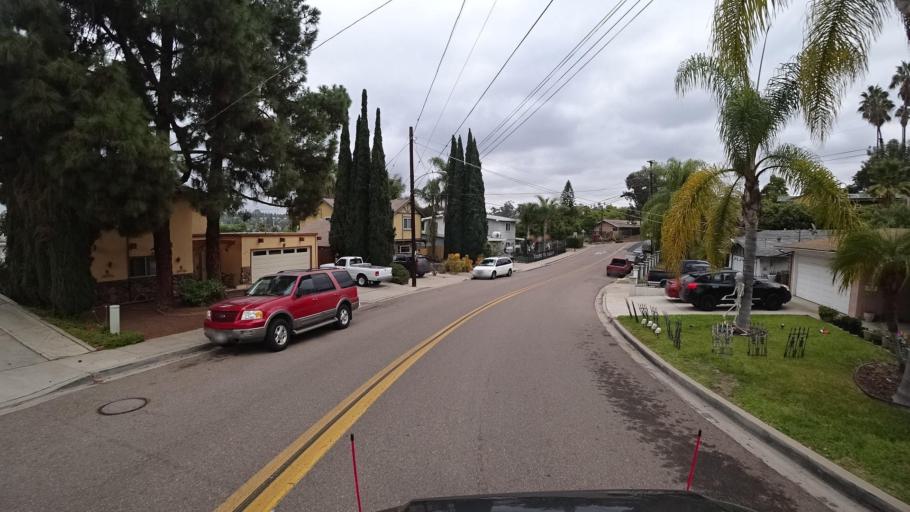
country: US
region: California
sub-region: San Diego County
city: Spring Valley
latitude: 32.7506
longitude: -117.0089
